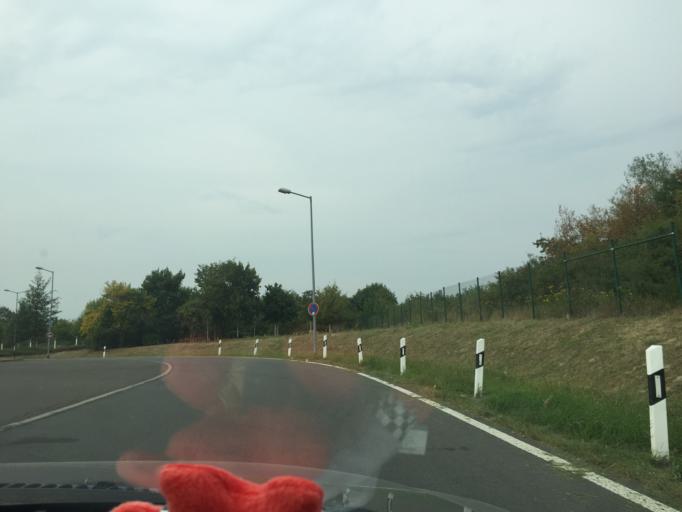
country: DE
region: Brandenburg
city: Neuenhagen
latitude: 52.5426
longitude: 13.6939
